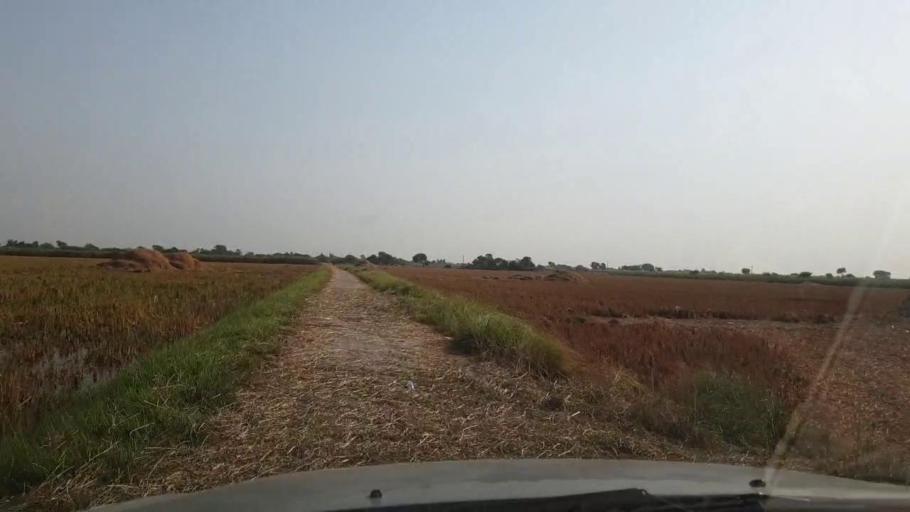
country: PK
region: Sindh
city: Bulri
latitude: 24.9196
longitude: 68.3125
